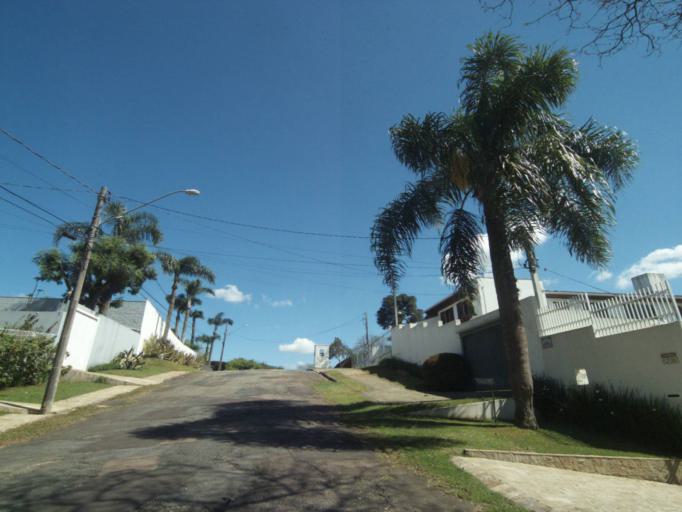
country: BR
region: Parana
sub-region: Curitiba
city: Curitiba
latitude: -25.3990
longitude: -49.2673
